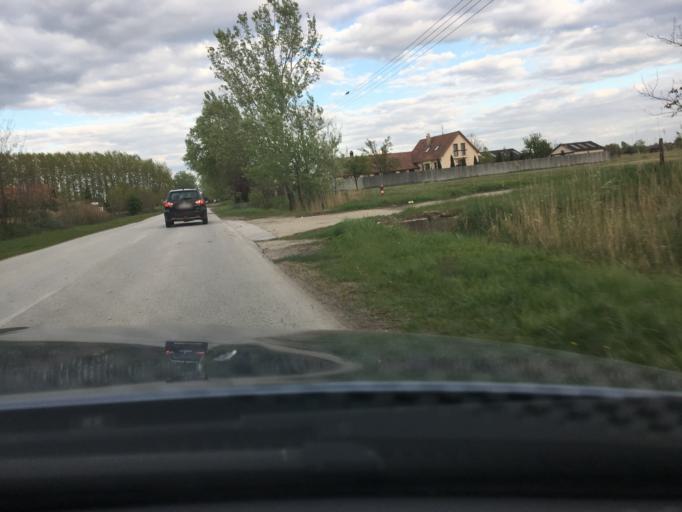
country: HU
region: Hajdu-Bihar
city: Debrecen
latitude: 47.5492
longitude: 21.6809
